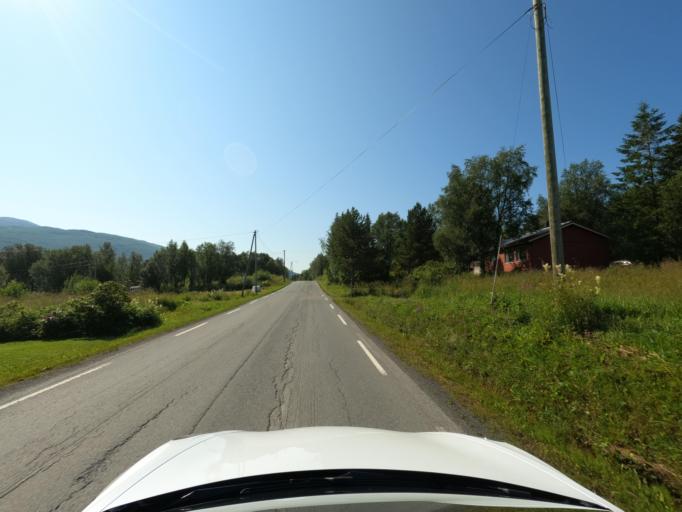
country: NO
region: Nordland
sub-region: Ballangen
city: Ballangen
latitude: 68.3536
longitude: 16.8639
